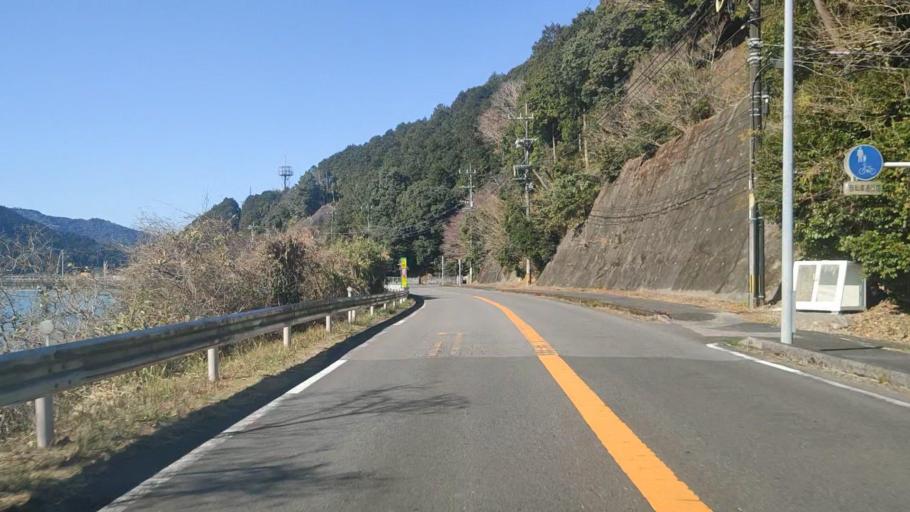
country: JP
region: Oita
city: Saiki
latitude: 32.9410
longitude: 131.9125
